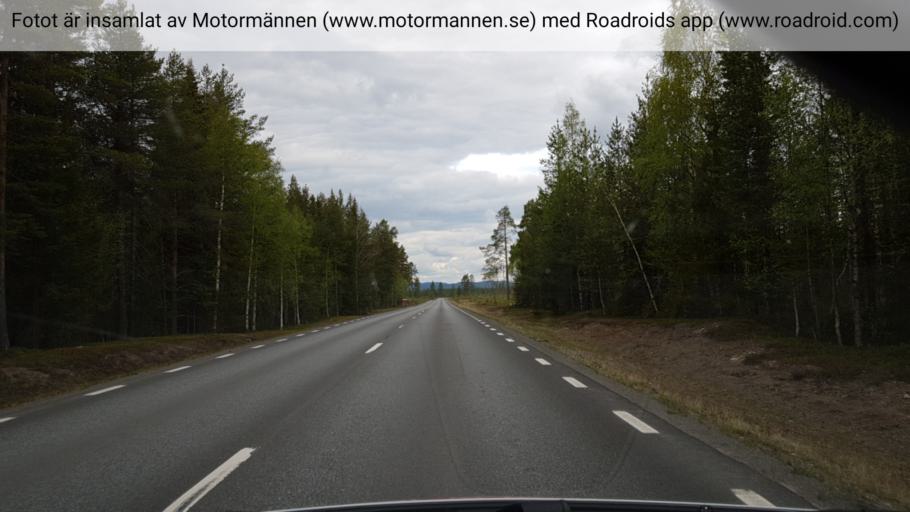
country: SE
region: Norrbotten
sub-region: Arvidsjaurs Kommun
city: Arvidsjaur
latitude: 65.4952
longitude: 19.3086
